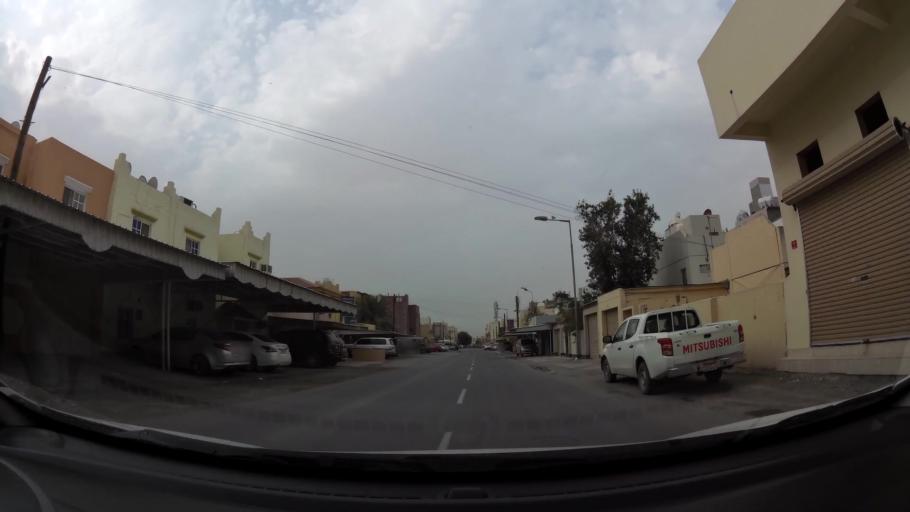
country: BH
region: Northern
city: Ar Rifa'
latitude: 26.1236
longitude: 50.5793
